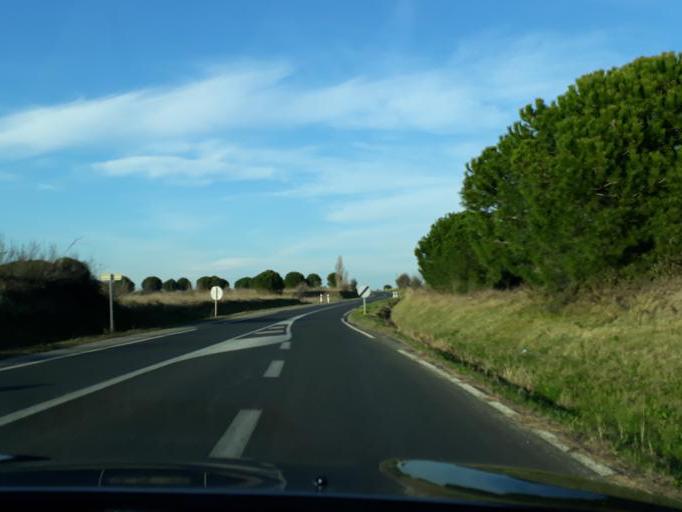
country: FR
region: Languedoc-Roussillon
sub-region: Departement de l'Herault
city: Marseillan
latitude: 43.3394
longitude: 3.5246
